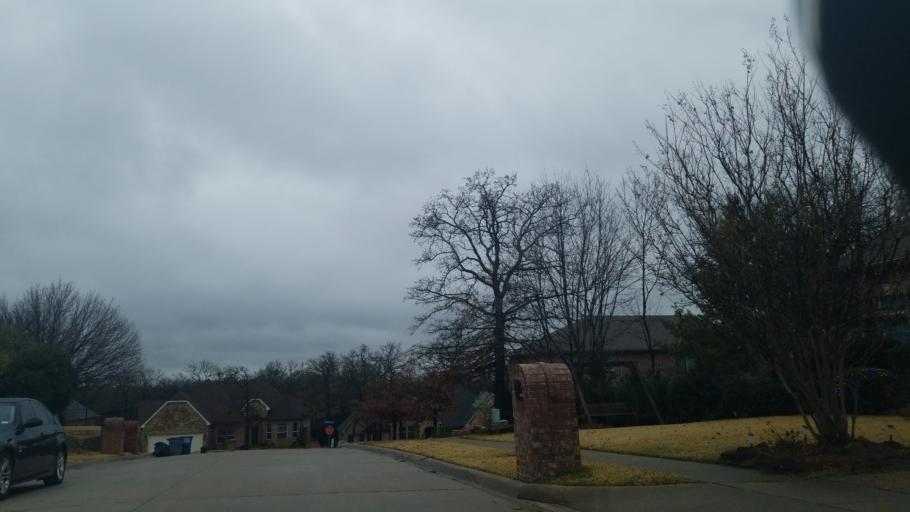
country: US
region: Texas
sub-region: Denton County
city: Corinth
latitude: 33.1455
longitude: -97.0892
